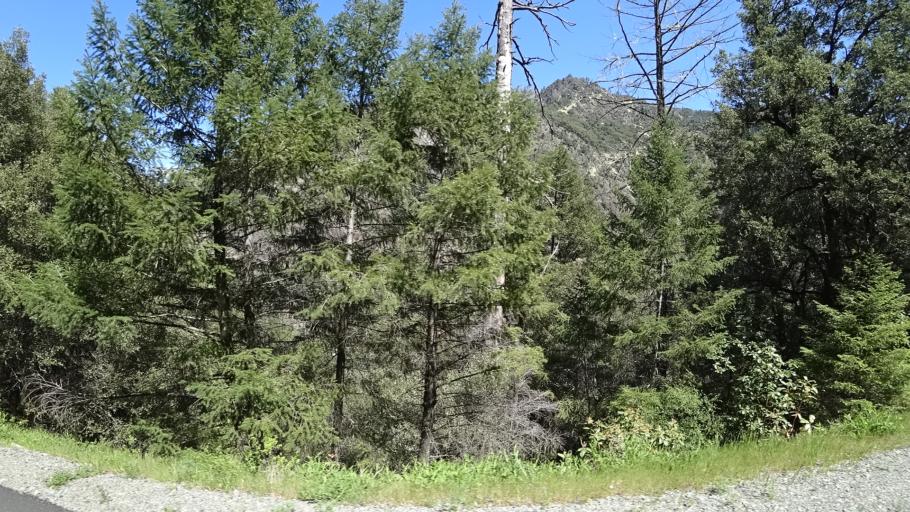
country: US
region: California
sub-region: Humboldt County
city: Willow Creek
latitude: 40.8198
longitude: -123.4811
